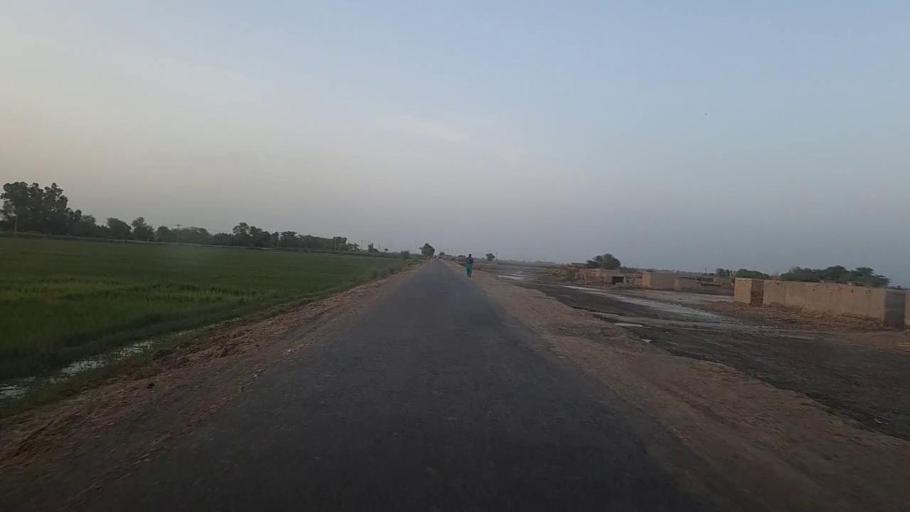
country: PK
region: Sindh
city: Radhan
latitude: 27.1389
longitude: 67.9337
